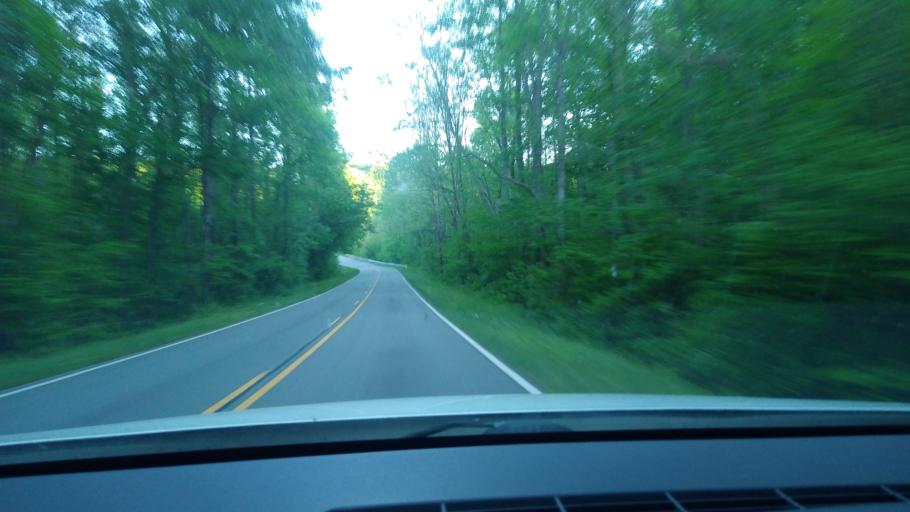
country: US
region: North Carolina
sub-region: Rockingham County
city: Reidsville
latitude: 36.3760
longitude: -79.5528
